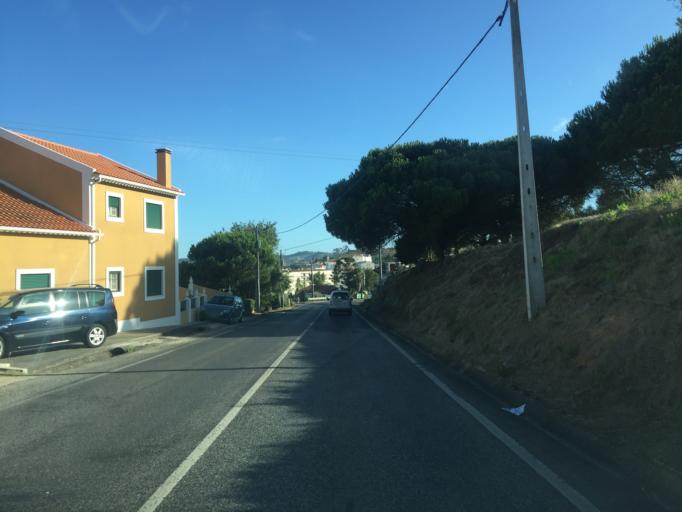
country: PT
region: Lisbon
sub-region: Torres Vedras
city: Torres Vedras
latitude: 39.1109
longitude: -9.2618
